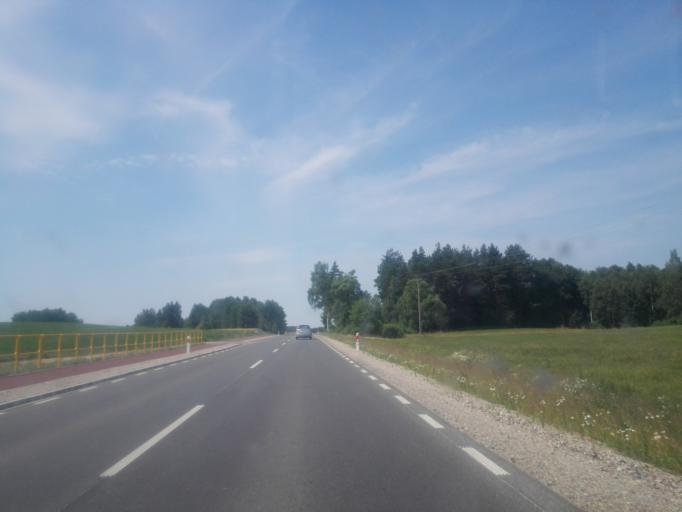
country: PL
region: Podlasie
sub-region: Powiat sejnenski
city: Krasnopol
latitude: 54.1085
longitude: 23.2718
